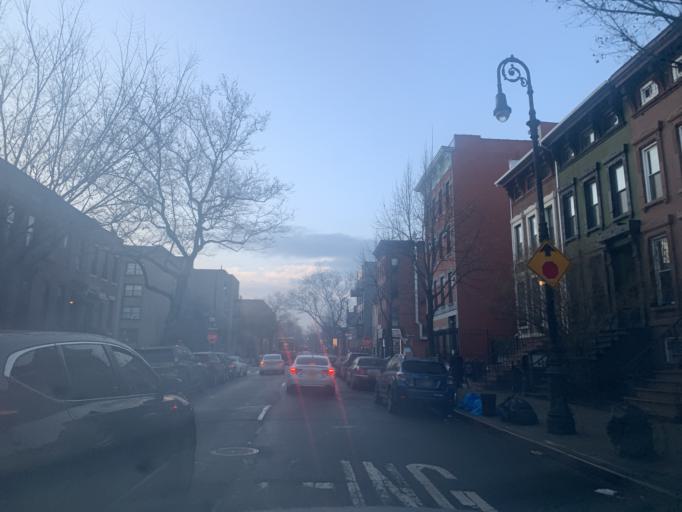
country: US
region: New York
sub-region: Kings County
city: Brooklyn
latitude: 40.6895
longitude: -73.9334
